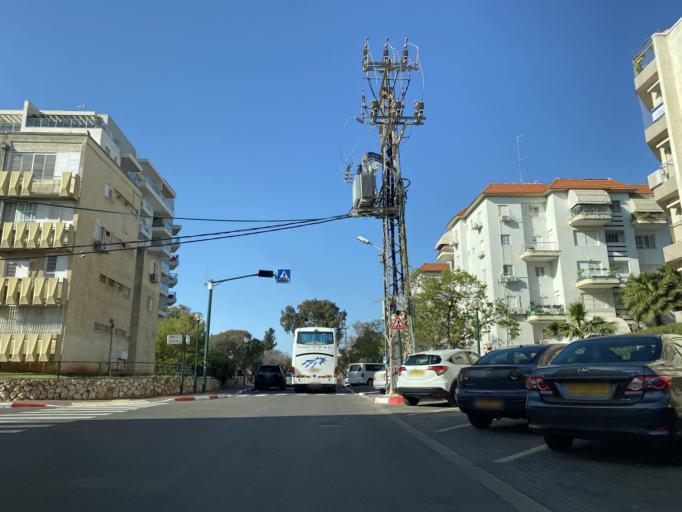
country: IL
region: Central District
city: Kfar Saba
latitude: 32.1797
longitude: 34.9157
